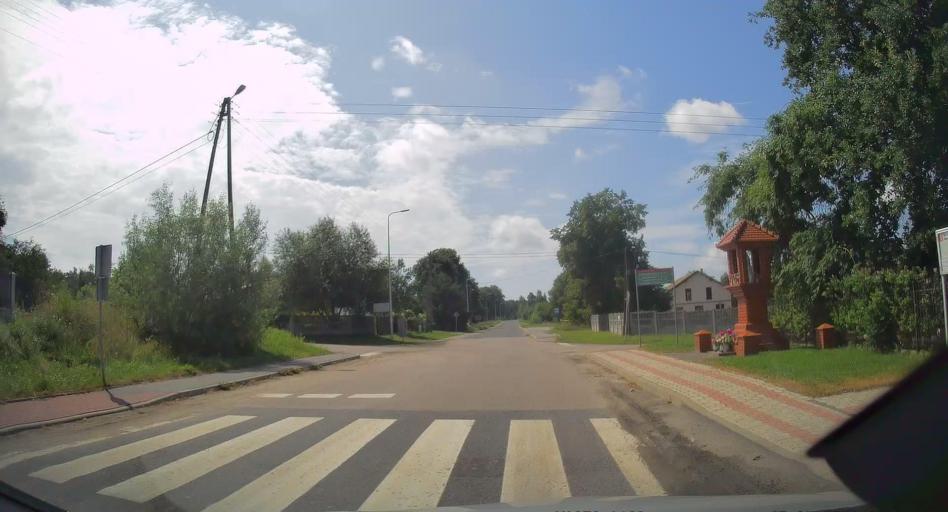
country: PL
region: Lodz Voivodeship
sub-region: Powiat rawski
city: Rawa Mazowiecka
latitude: 51.7073
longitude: 20.2152
